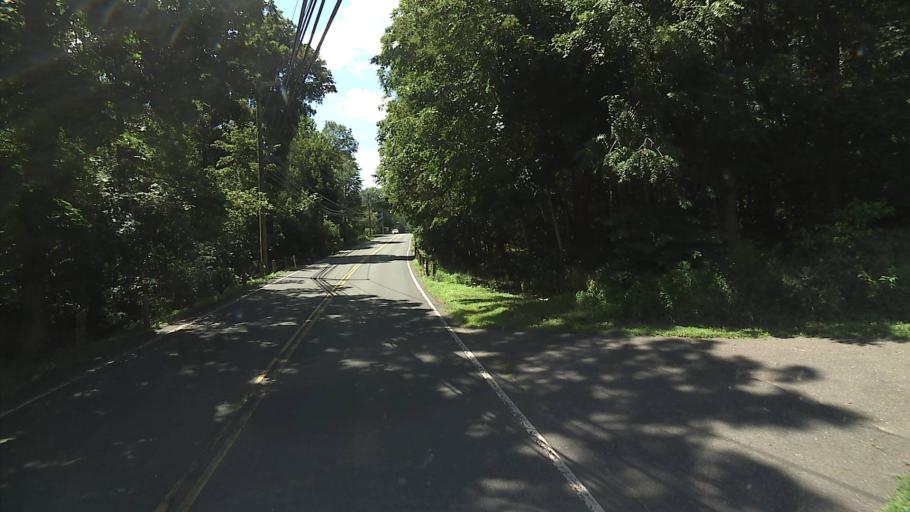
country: US
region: Connecticut
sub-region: Hartford County
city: Suffield Depot
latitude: 41.9929
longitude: -72.7129
